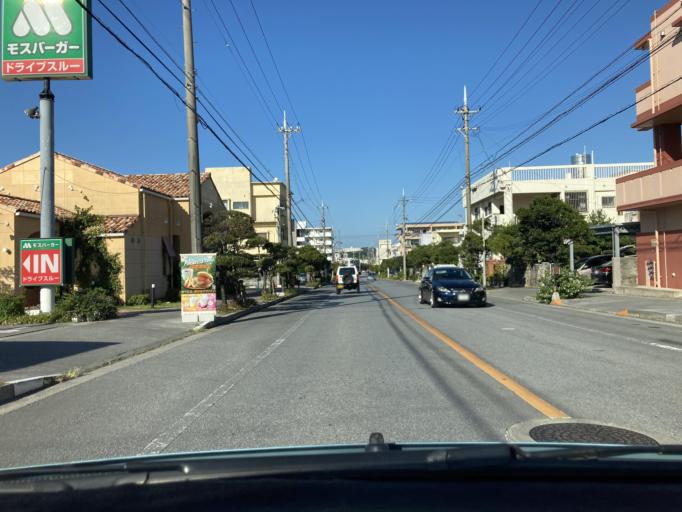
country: JP
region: Okinawa
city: Ginowan
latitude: 26.2819
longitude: 127.7820
